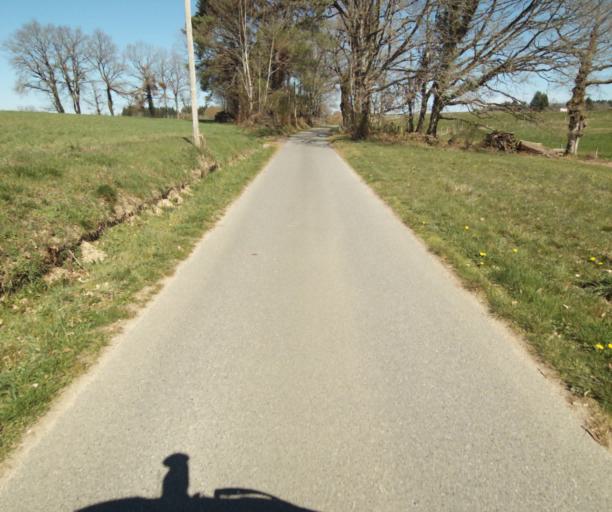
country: FR
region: Limousin
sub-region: Departement de la Correze
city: Chamboulive
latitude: 45.4587
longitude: 1.7093
